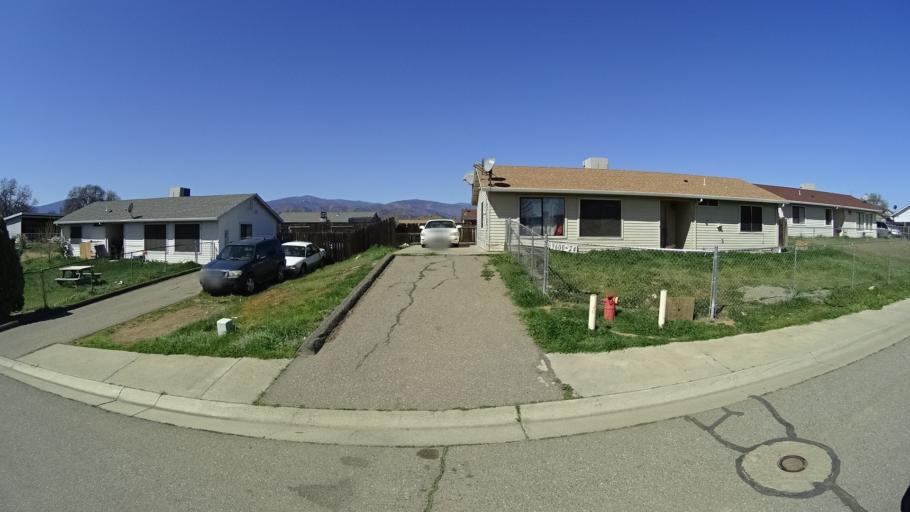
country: US
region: California
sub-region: Glenn County
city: Orland
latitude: 39.6746
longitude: -122.5205
